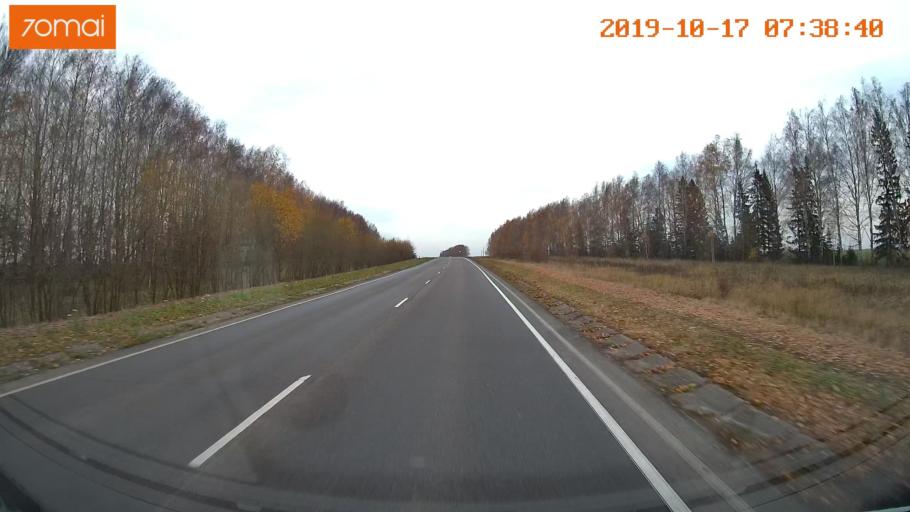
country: RU
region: Vladimir
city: Yur'yev-Pol'skiy
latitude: 56.4573
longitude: 39.8684
